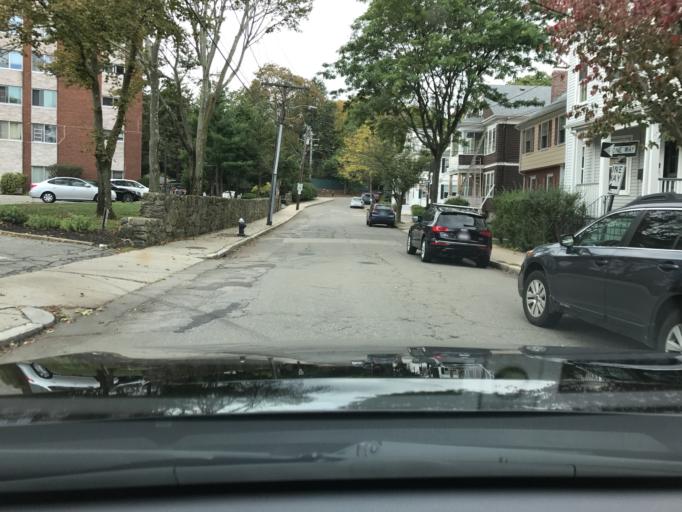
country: US
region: Massachusetts
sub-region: Norfolk County
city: Brookline
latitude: 42.3263
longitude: -71.1254
